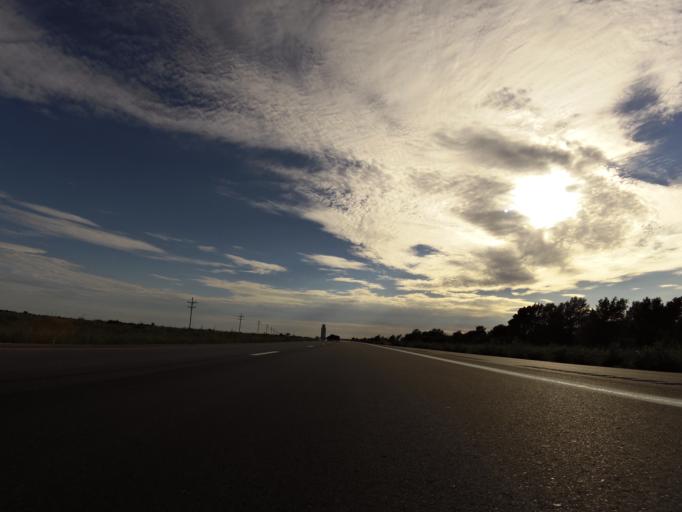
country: US
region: Kansas
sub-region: Reno County
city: South Hutchinson
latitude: 38.0118
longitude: -98.0038
